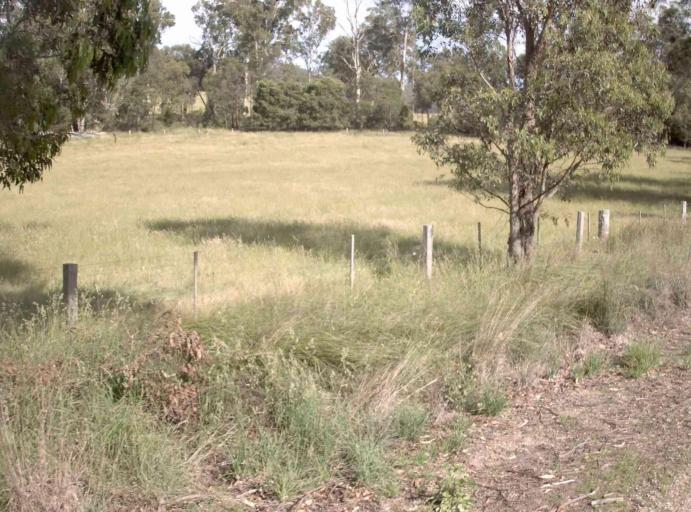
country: AU
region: Victoria
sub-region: East Gippsland
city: Lakes Entrance
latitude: -37.5390
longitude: 148.1481
